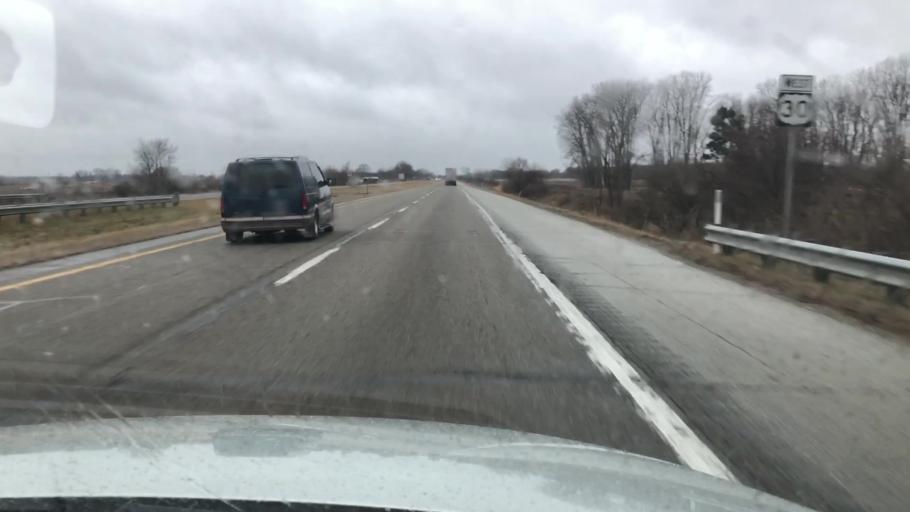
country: US
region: Indiana
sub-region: Starke County
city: Knox
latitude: 41.3940
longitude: -86.6298
